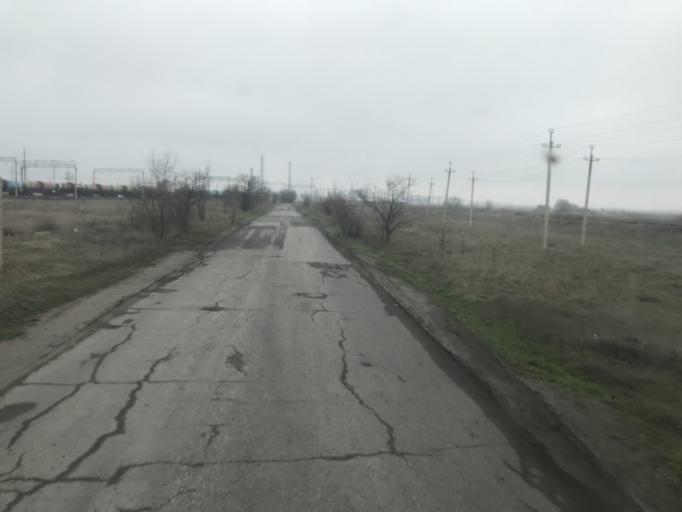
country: RU
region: Volgograd
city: Svetlyy Yar
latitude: 48.4932
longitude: 44.6562
